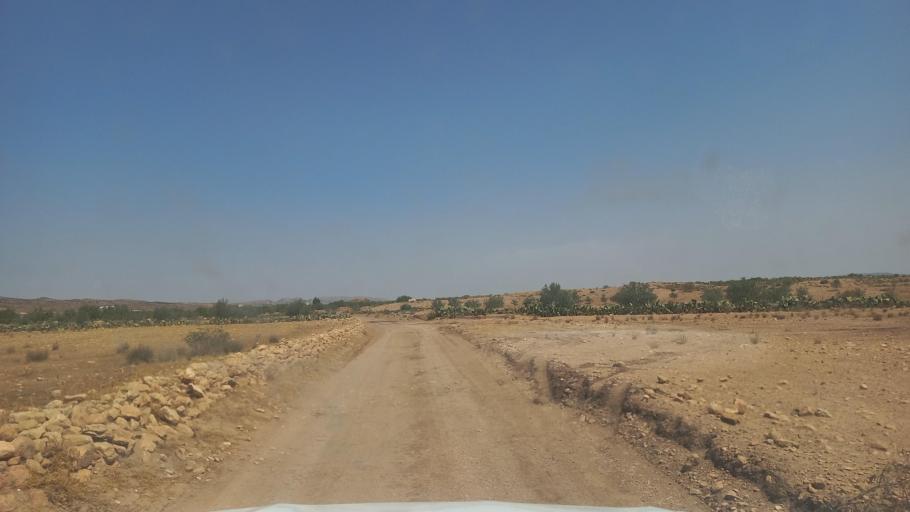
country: TN
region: Al Qasrayn
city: Kasserine
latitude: 35.2913
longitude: 8.9530
